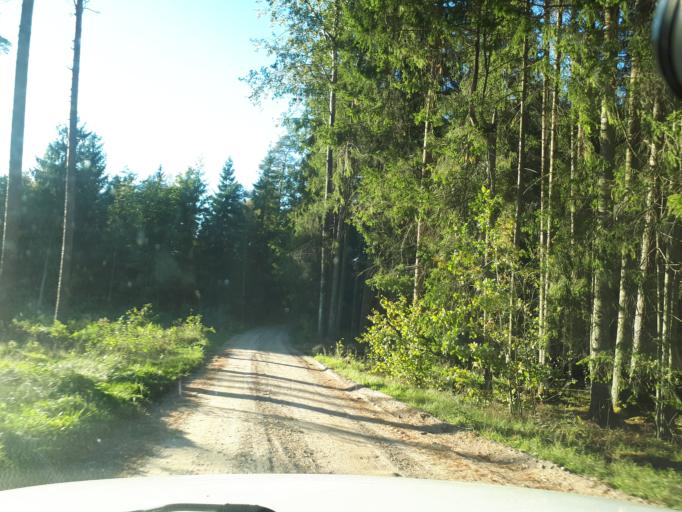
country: LT
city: Kulautuva
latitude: 54.9319
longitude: 23.5852
